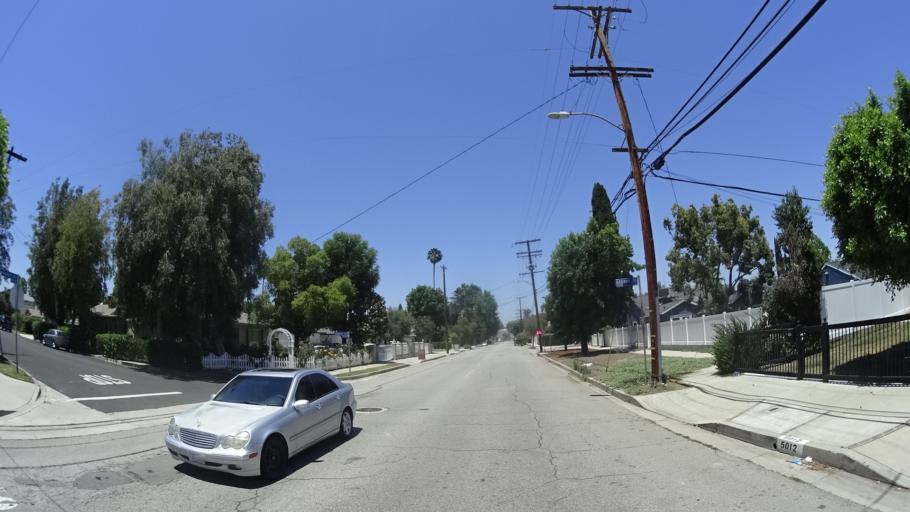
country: US
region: California
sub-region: Los Angeles County
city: Sherman Oaks
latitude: 34.1615
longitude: -118.4749
